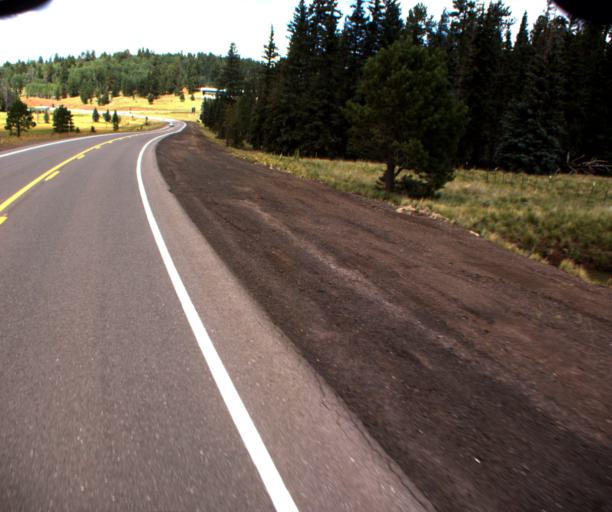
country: US
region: Arizona
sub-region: Apache County
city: Eagar
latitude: 34.0010
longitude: -109.5573
